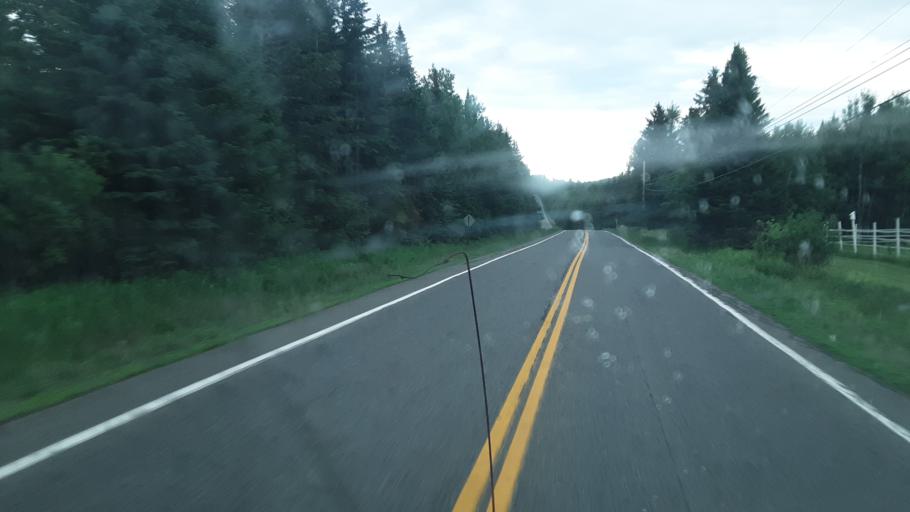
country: US
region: Maine
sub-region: Aroostook County
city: Presque Isle
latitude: 46.4772
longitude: -68.3878
